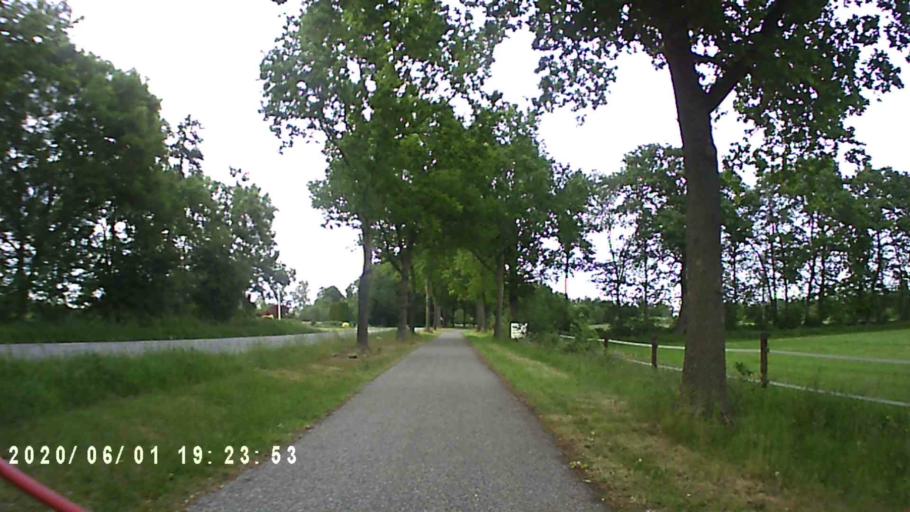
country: NL
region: Friesland
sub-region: Gemeente Achtkarspelen
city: Drogeham
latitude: 53.2043
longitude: 6.1272
